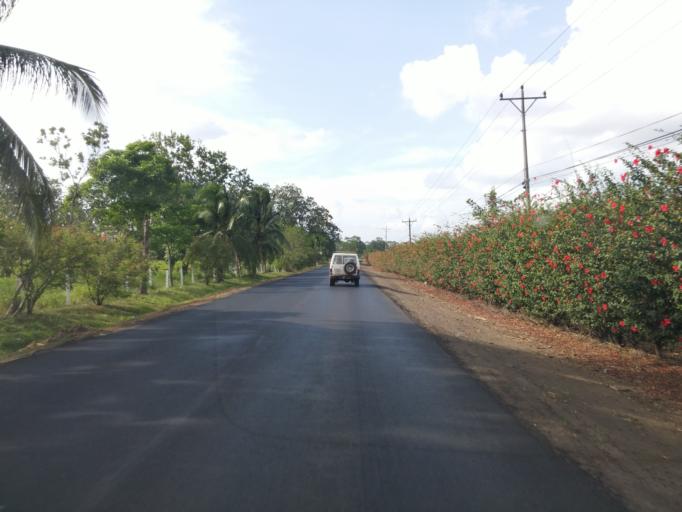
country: CR
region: Alajuela
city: Quesada
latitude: 10.4339
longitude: -84.4678
